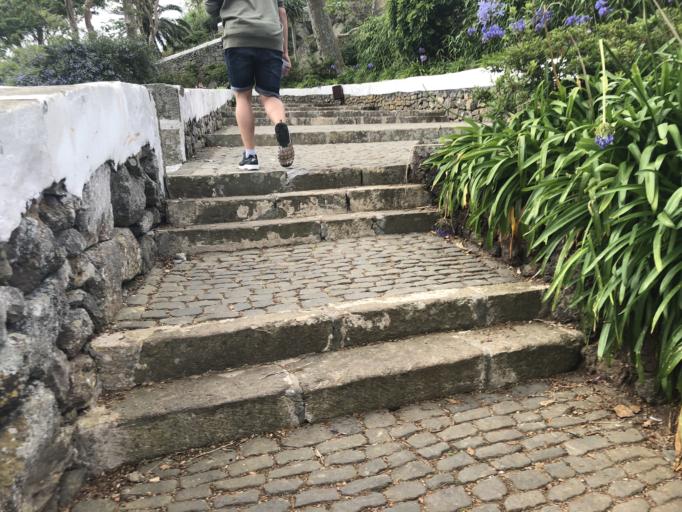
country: PT
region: Azores
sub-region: Angra do Heroismo
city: Angra do Heroismo
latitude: 38.6578
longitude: -27.2180
